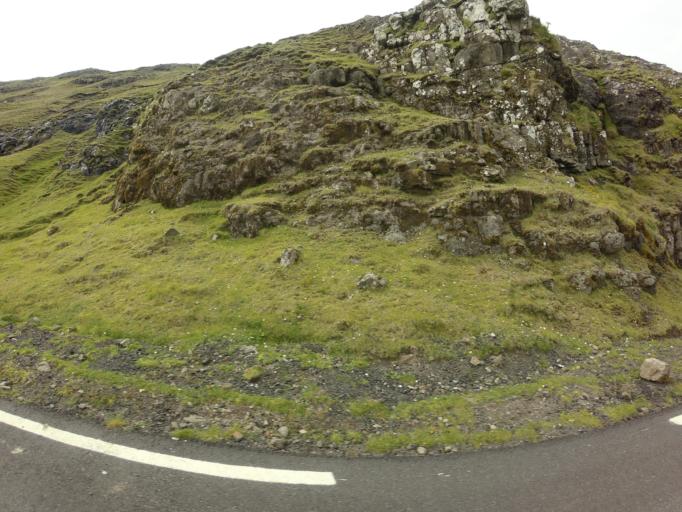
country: FO
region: Suduroy
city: Tvoroyri
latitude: 61.6248
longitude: -6.9395
